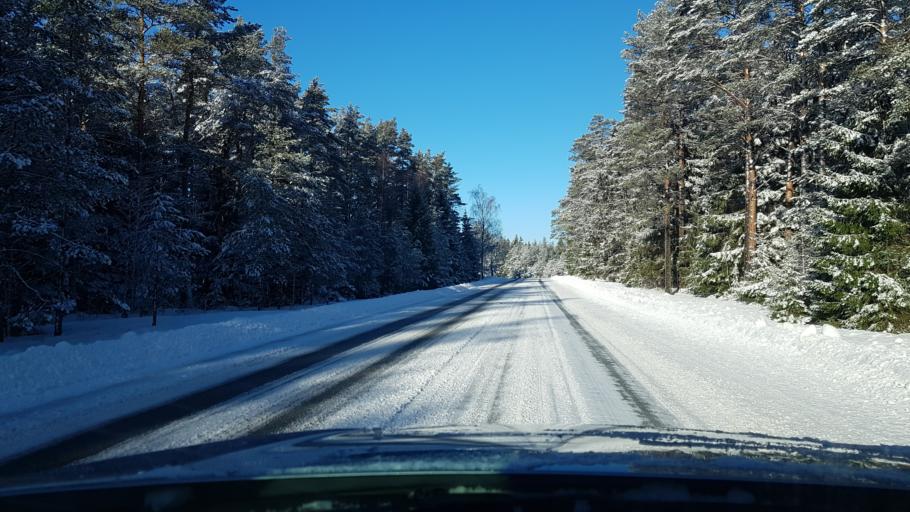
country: EE
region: Hiiumaa
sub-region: Kaerdla linn
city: Kardla
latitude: 58.9339
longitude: 22.7825
